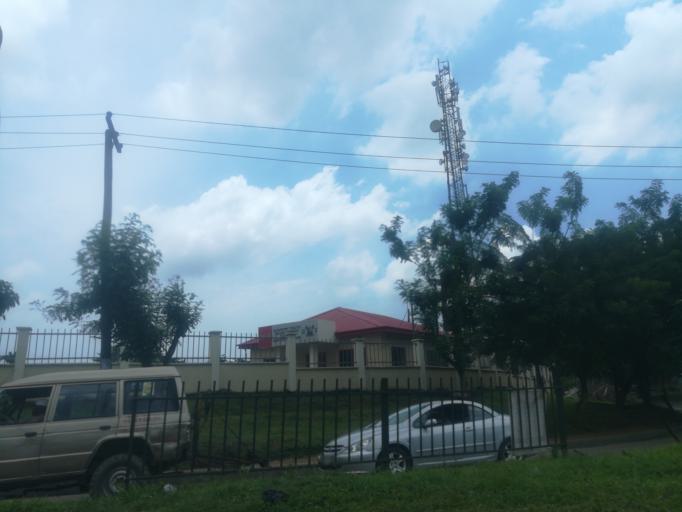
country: NG
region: Lagos
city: Somolu
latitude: 6.5510
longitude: 3.3913
